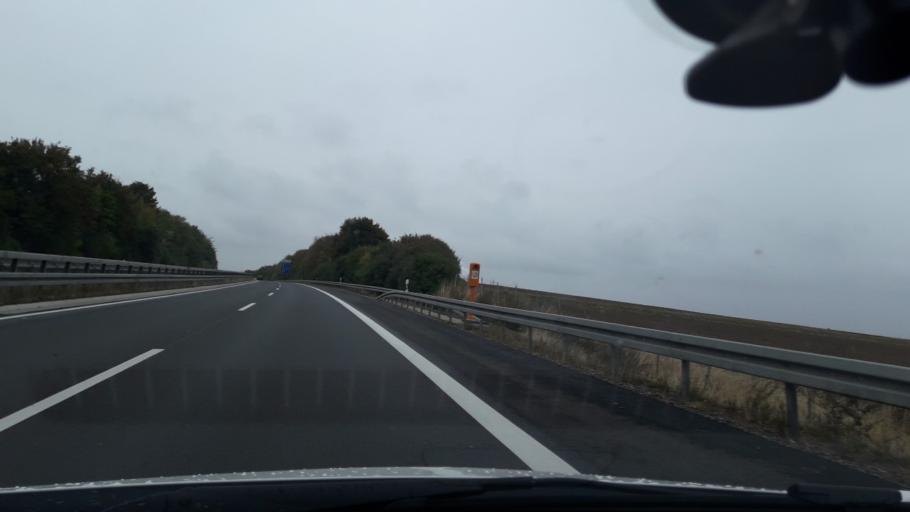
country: DE
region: Lower Saxony
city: Schladen
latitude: 51.9965
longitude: 10.5522
